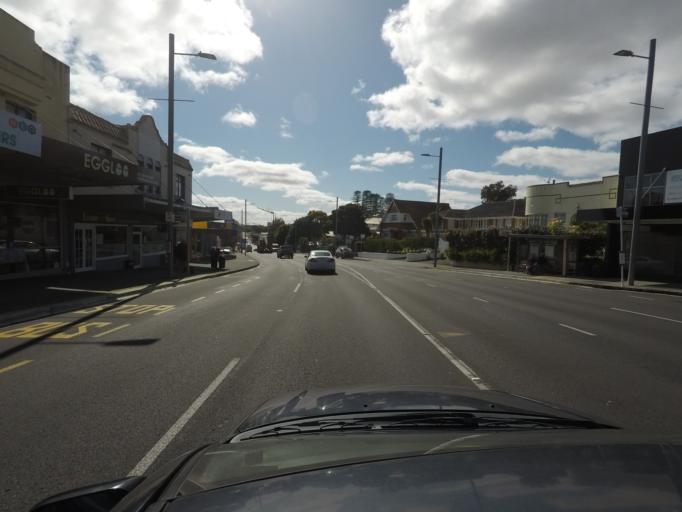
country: NZ
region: Auckland
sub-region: Auckland
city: Rosebank
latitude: -36.8838
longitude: 174.7160
